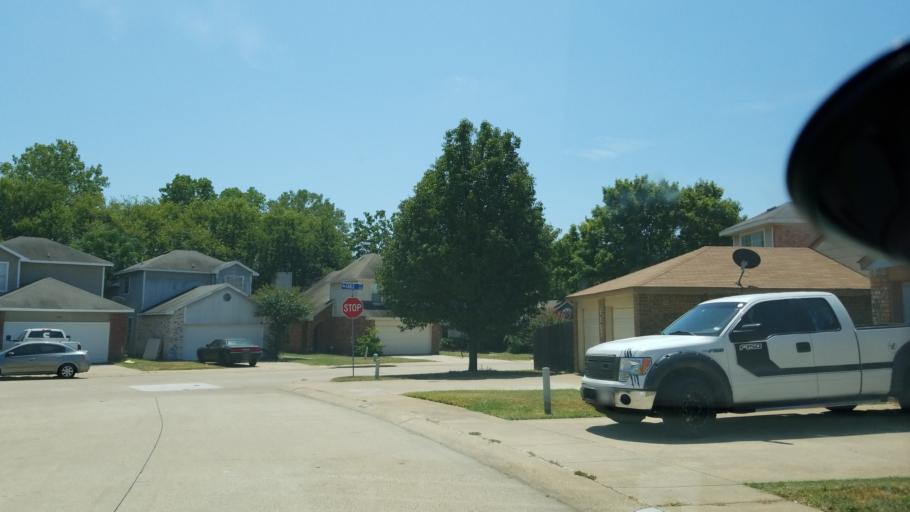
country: US
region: Texas
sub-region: Dallas County
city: Duncanville
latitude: 32.6377
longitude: -96.8908
